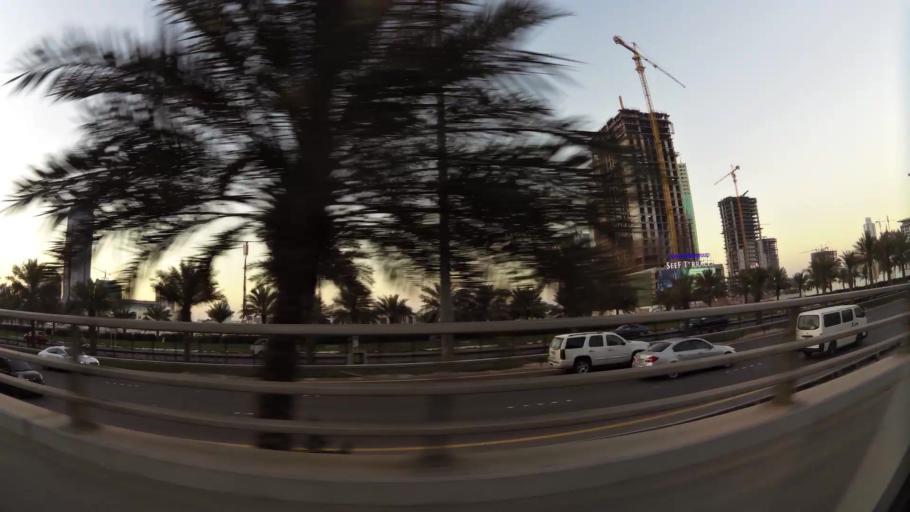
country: BH
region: Manama
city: Jidd Hafs
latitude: 26.2314
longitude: 50.5466
